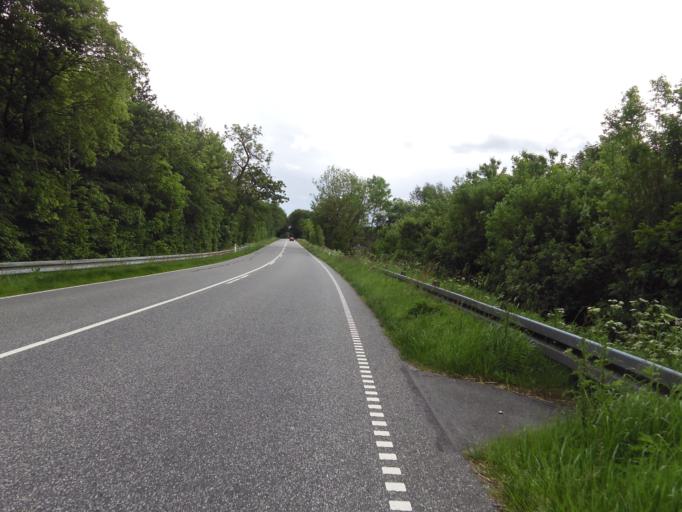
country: DK
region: South Denmark
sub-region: Haderslev Kommune
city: Gram
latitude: 55.3096
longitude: 9.0630
